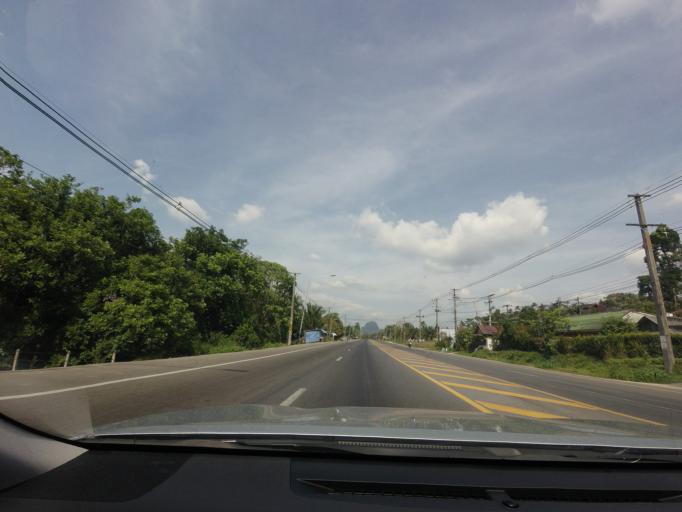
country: TH
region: Phangnga
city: Ban Ao Nang
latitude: 8.0858
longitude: 98.8064
